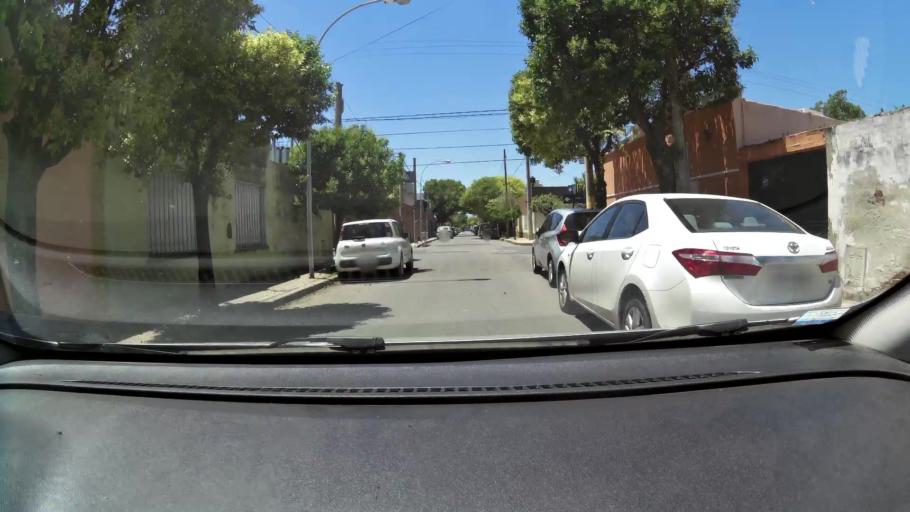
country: AR
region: Cordoba
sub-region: Departamento de Capital
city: Cordoba
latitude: -31.3865
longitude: -64.1353
